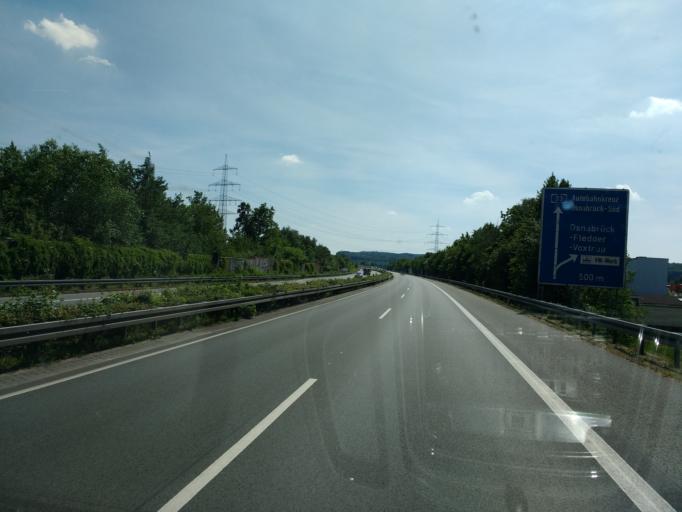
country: DE
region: Lower Saxony
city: Osnabrueck
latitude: 52.2610
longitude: 8.0963
